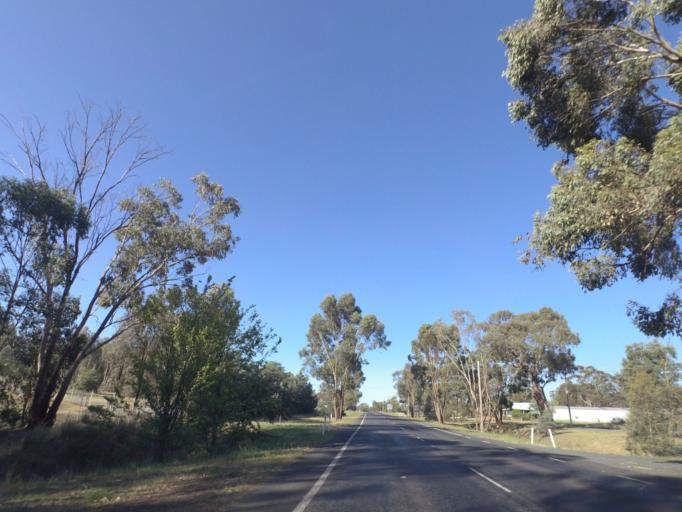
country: AU
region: New South Wales
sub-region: Wagga Wagga
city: Forest Hill
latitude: -35.2731
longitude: 147.7423
